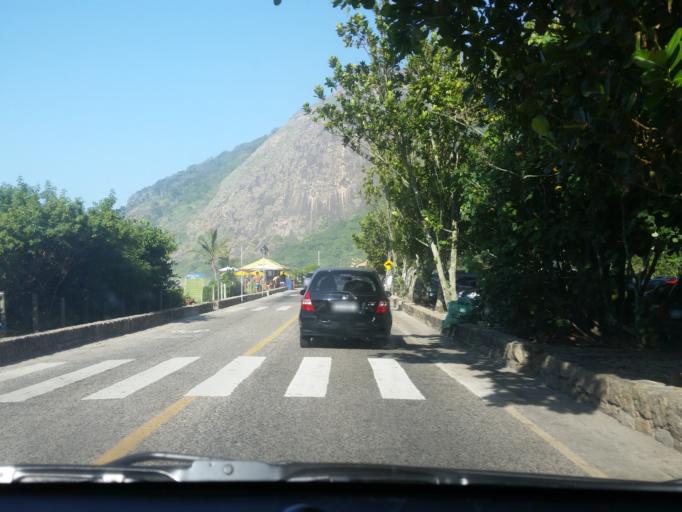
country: BR
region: Rio de Janeiro
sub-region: Nilopolis
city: Nilopolis
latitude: -23.0398
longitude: -43.5044
